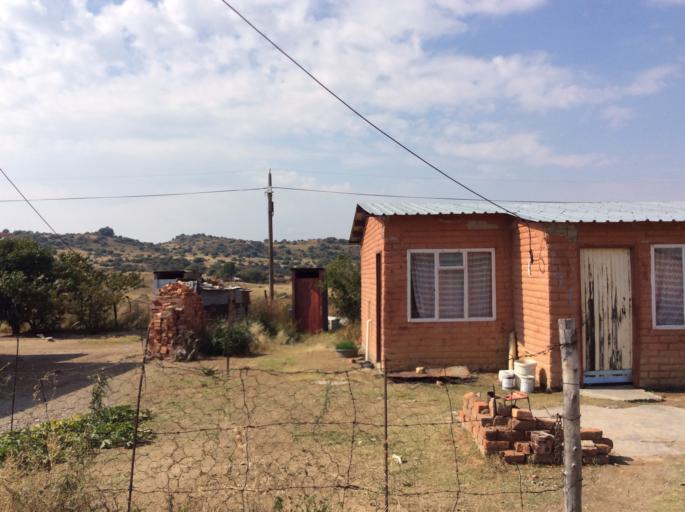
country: LS
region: Mafeteng
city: Mafeteng
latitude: -29.9819
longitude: 27.0098
